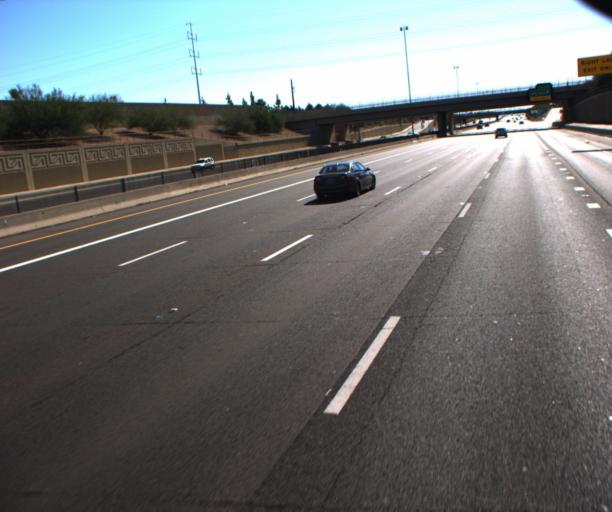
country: US
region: Arizona
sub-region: Maricopa County
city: Guadalupe
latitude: 33.3854
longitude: -111.9454
